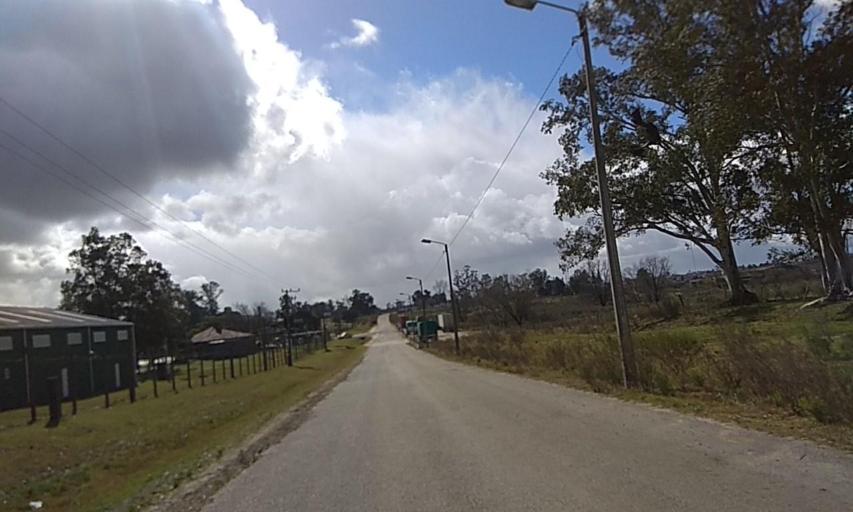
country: UY
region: Florida
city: Florida
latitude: -34.1138
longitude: -56.2276
